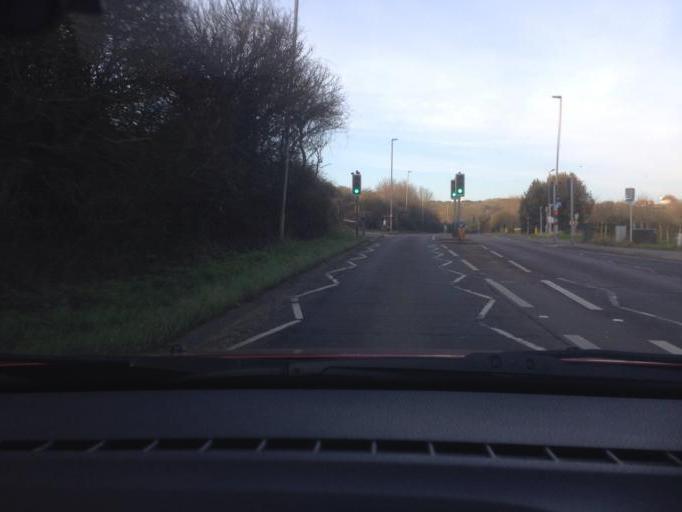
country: GB
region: England
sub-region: East Sussex
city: Newhaven
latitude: 50.7905
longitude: 0.0357
